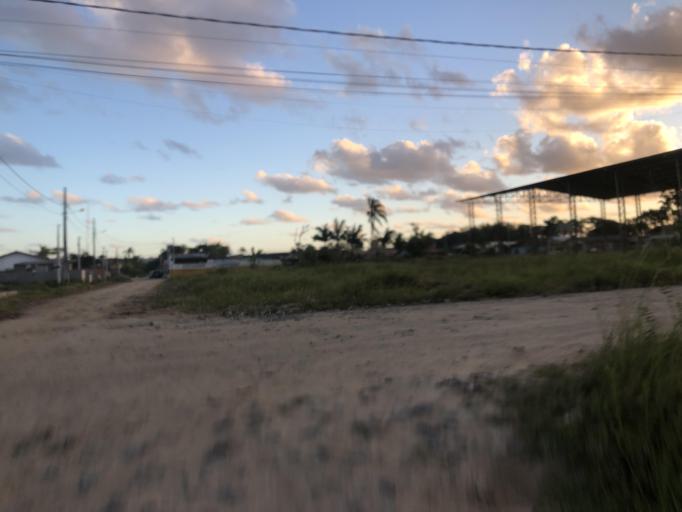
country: BR
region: Santa Catarina
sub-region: Sao Francisco Do Sul
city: Sao Francisco do Sul
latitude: -26.2216
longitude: -48.5313
